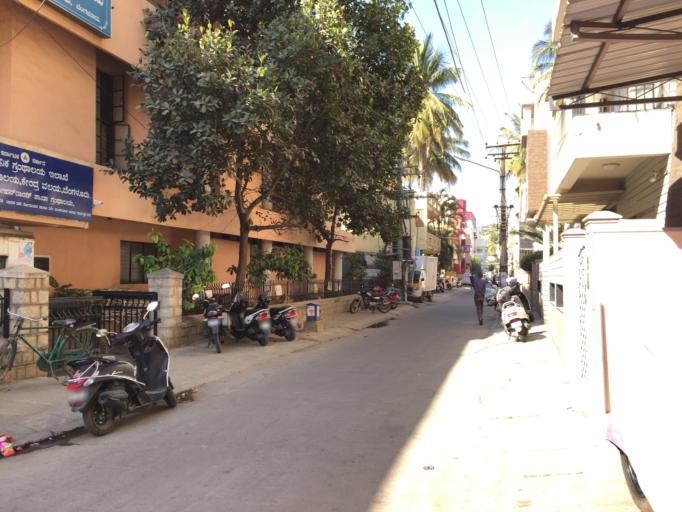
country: IN
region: Karnataka
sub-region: Bangalore Urban
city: Bangalore
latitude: 12.9591
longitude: 77.5923
